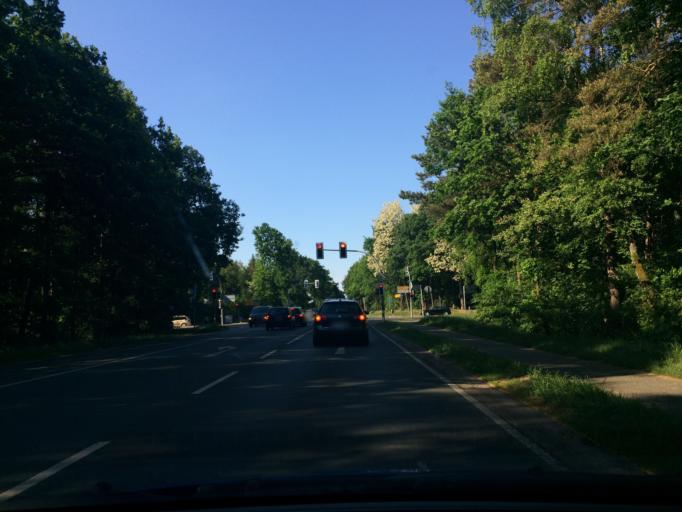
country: DE
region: Lower Saxony
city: Soltau
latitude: 53.0262
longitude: 9.8504
